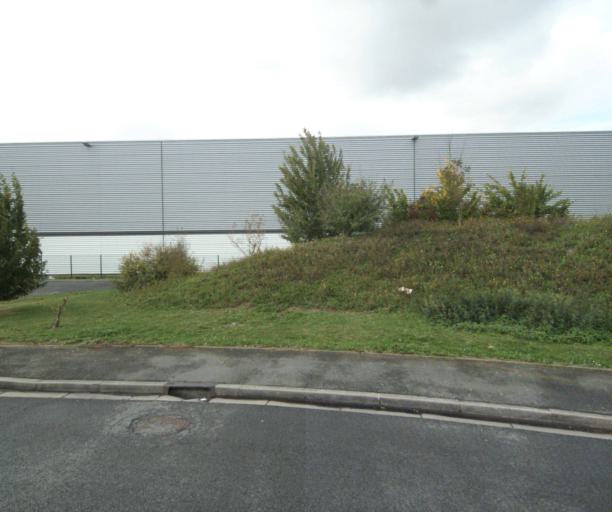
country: FR
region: Nord-Pas-de-Calais
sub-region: Departement du Nord
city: Houplines
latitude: 50.6828
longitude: 2.9129
